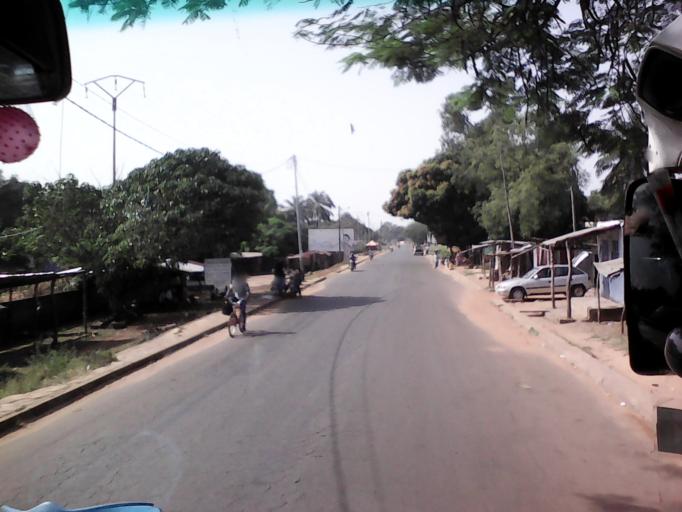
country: TG
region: Centrale
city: Sokode
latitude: 8.9746
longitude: 1.1383
